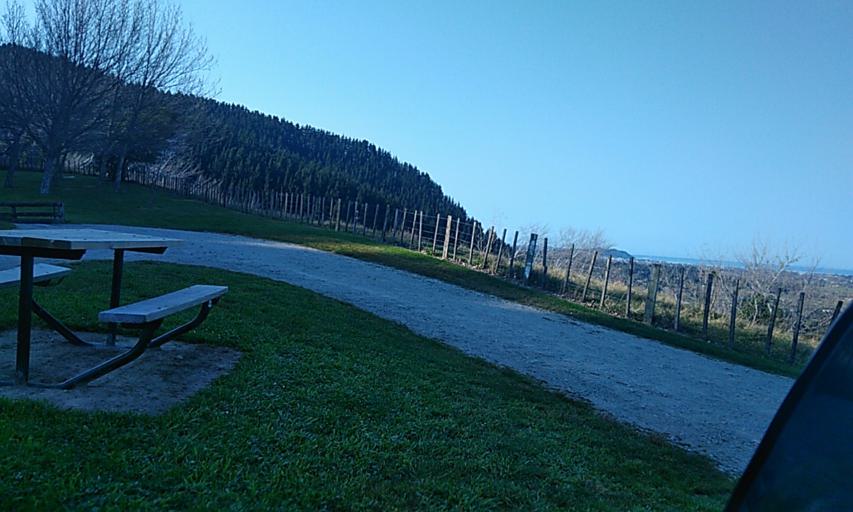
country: NZ
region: Gisborne
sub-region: Gisborne District
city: Gisborne
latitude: -38.5940
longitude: 177.9753
